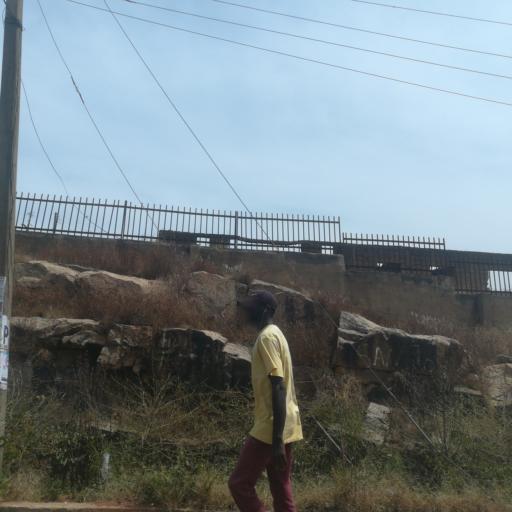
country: NG
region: Plateau
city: Jos
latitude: 9.8950
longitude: 8.8646
